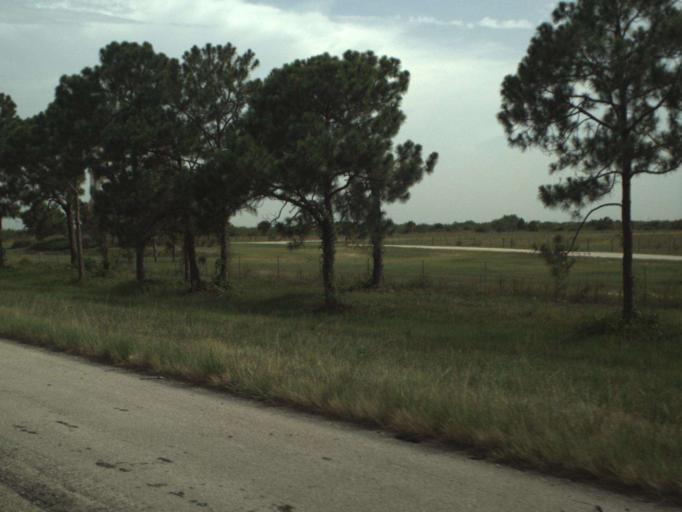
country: US
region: Florida
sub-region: Saint Lucie County
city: Port Saint Lucie
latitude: 27.2572
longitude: -80.4197
